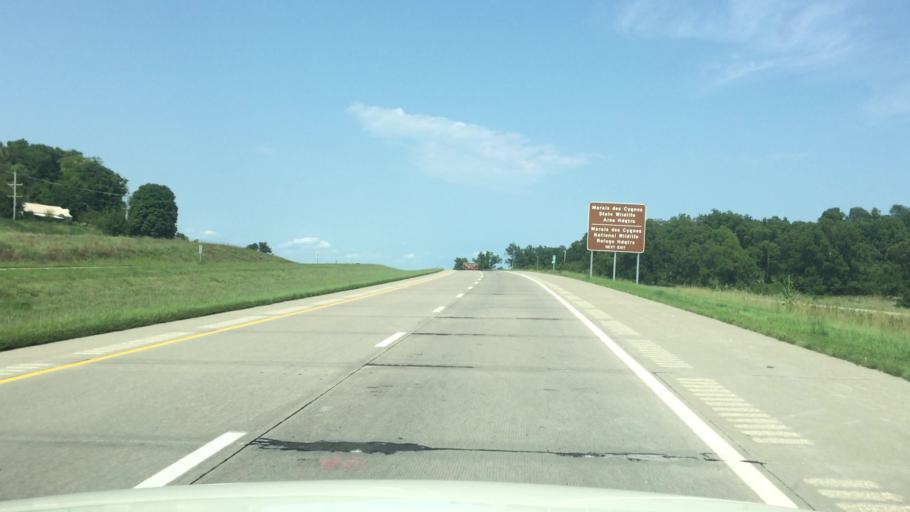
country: US
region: Kansas
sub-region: Linn County
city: Pleasanton
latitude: 38.2545
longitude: -94.6791
